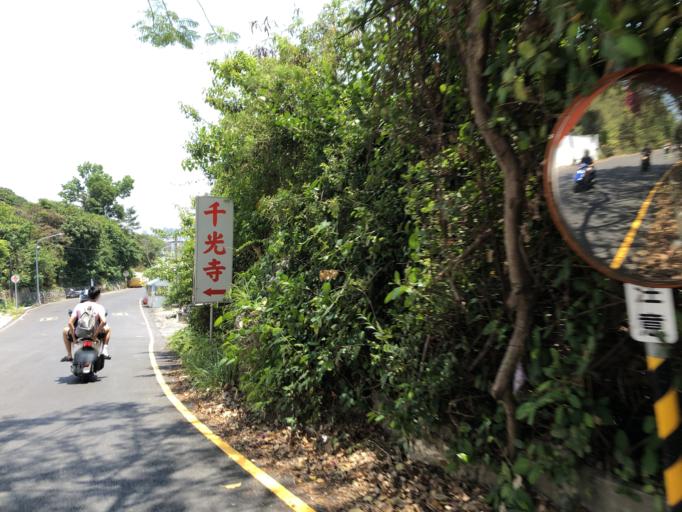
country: TW
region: Kaohsiung
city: Kaohsiung
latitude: 22.6251
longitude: 120.2728
